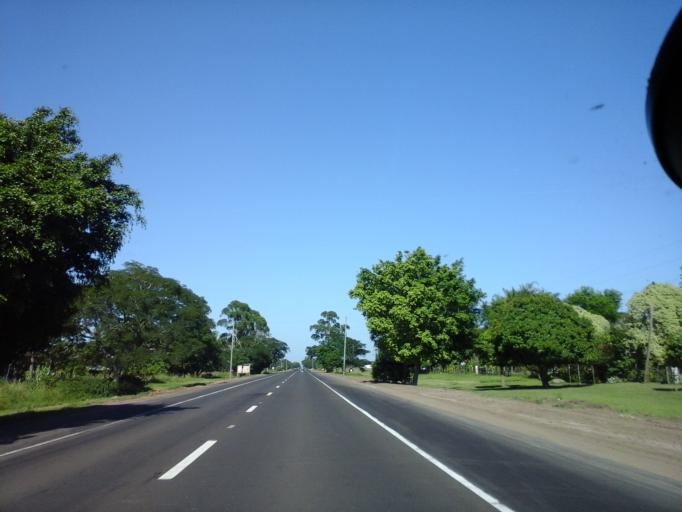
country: AR
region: Corrientes
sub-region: Departamento de Itati
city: Itati
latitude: -27.3666
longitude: -58.3311
